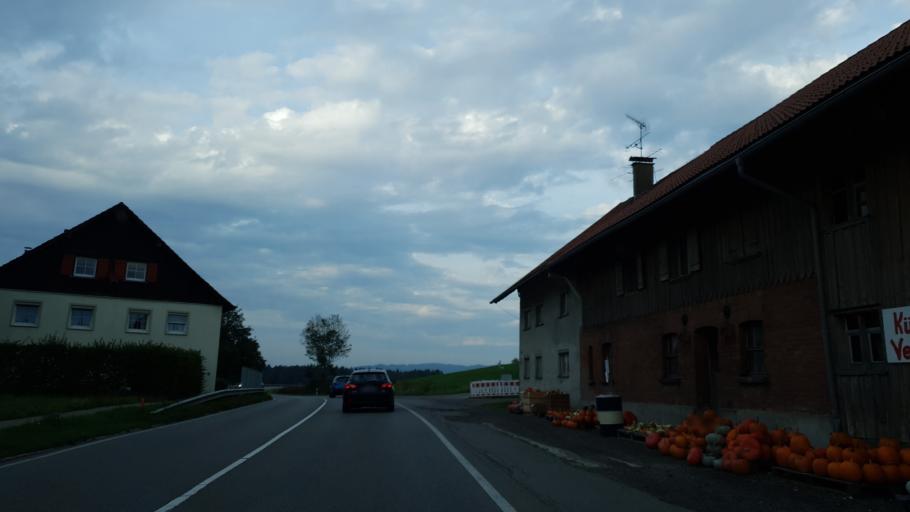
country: DE
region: Bavaria
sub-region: Swabia
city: Gestratz
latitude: 47.6813
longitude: 9.9982
